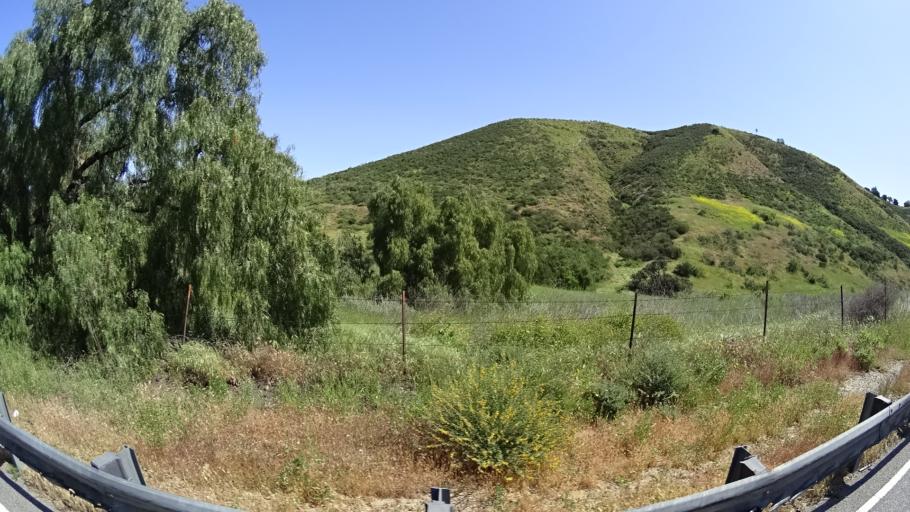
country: US
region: California
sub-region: Ventura County
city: Moorpark
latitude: 34.2393
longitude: -118.8622
